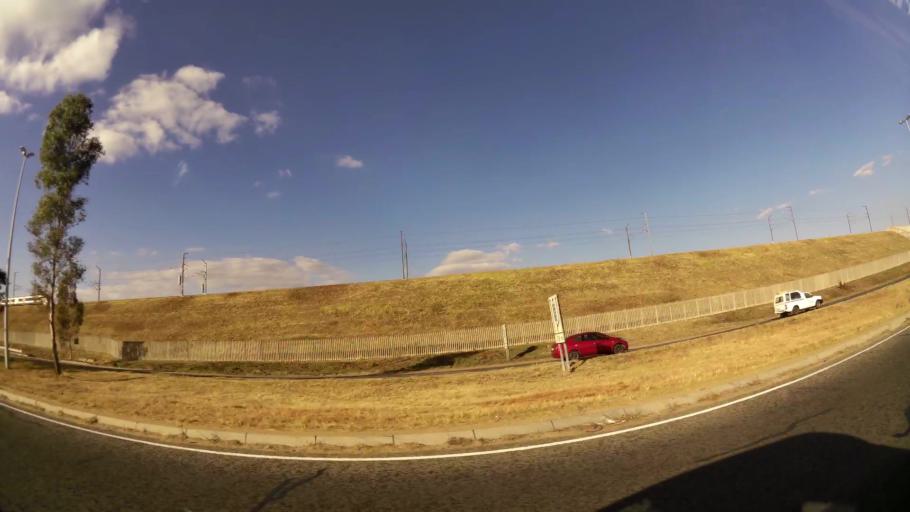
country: ZA
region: Gauteng
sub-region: City of Johannesburg Metropolitan Municipality
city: Midrand
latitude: -25.9864
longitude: 28.1318
